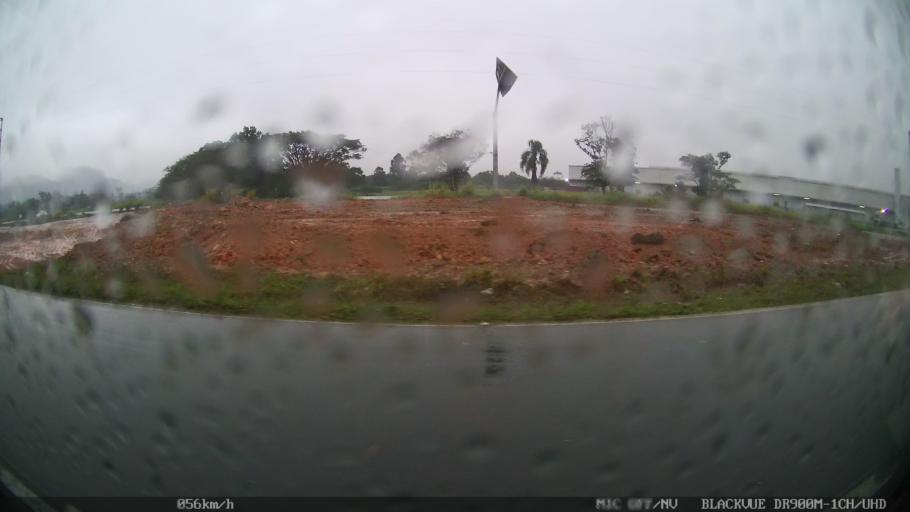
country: BR
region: Santa Catarina
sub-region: Navegantes
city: Navegantes
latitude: -26.8703
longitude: -48.6734
